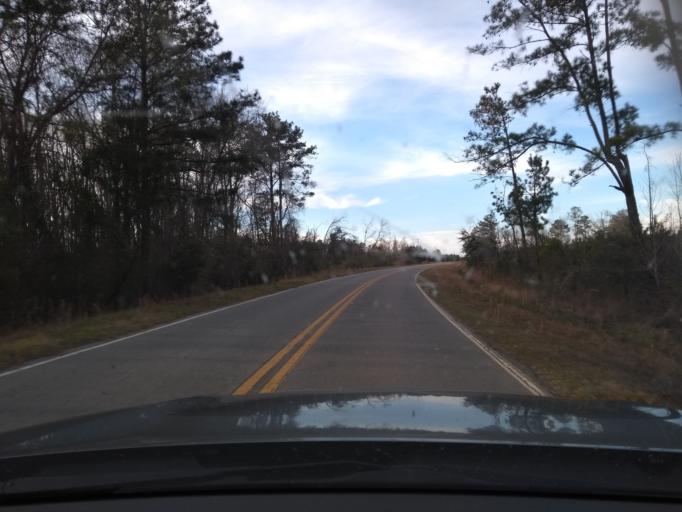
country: US
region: Georgia
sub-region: Evans County
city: Claxton
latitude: 32.2269
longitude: -81.7700
